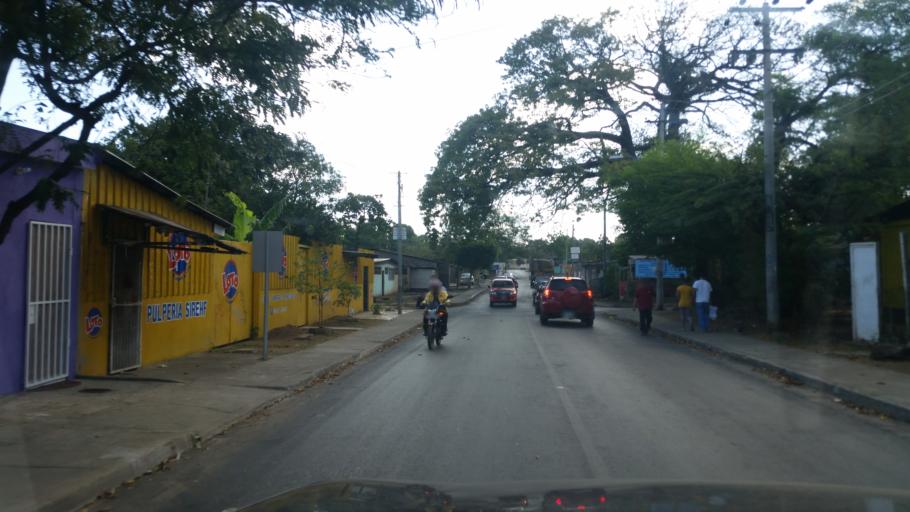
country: NI
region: Managua
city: Managua
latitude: 12.1370
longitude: -86.2341
